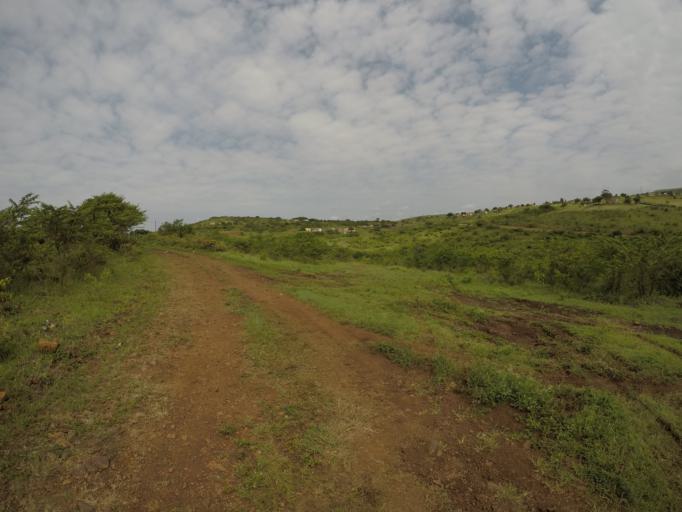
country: ZA
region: KwaZulu-Natal
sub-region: uThungulu District Municipality
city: Empangeni
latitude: -28.6217
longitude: 31.9098
